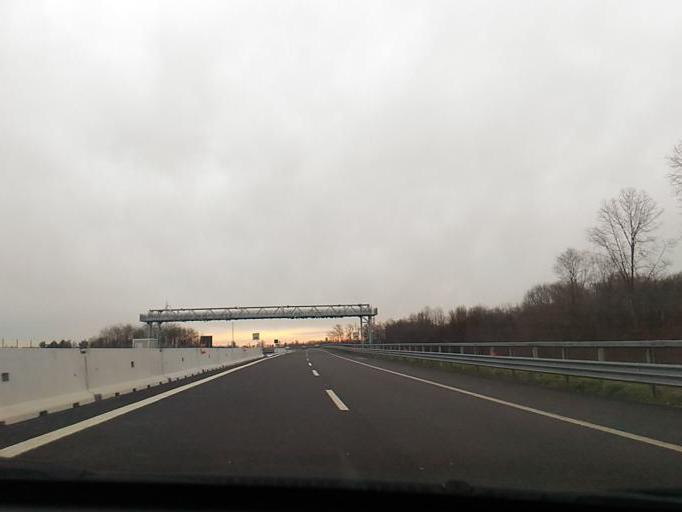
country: IT
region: Lombardy
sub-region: Provincia di Como
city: Mozzate
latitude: 45.6623
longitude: 8.9443
